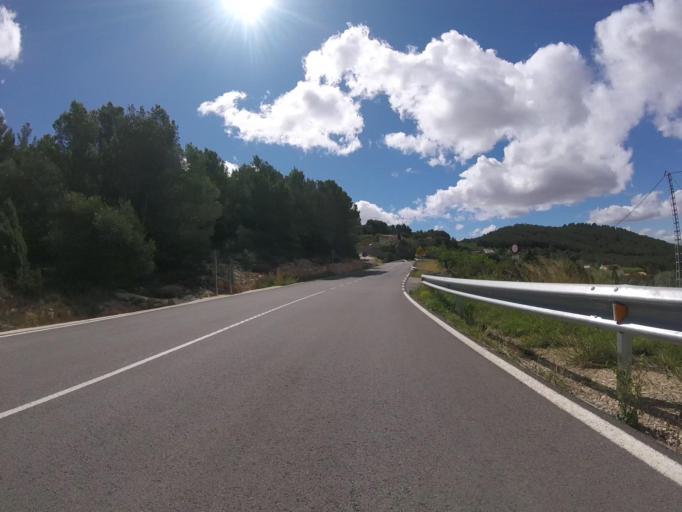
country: ES
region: Valencia
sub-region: Provincia de Castello
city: Culla
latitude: 40.2789
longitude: -0.1119
